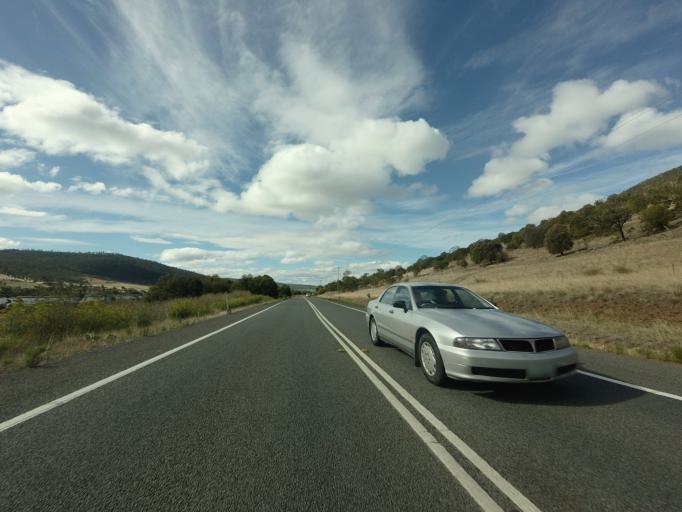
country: AU
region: Tasmania
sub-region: Glenorchy
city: Granton
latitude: -42.7597
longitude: 147.1478
